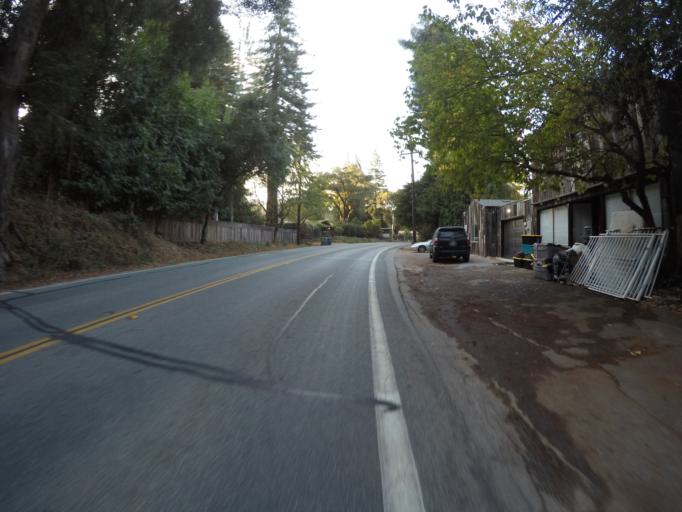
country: US
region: California
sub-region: Santa Cruz County
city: Felton
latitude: 37.0404
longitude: -122.0714
